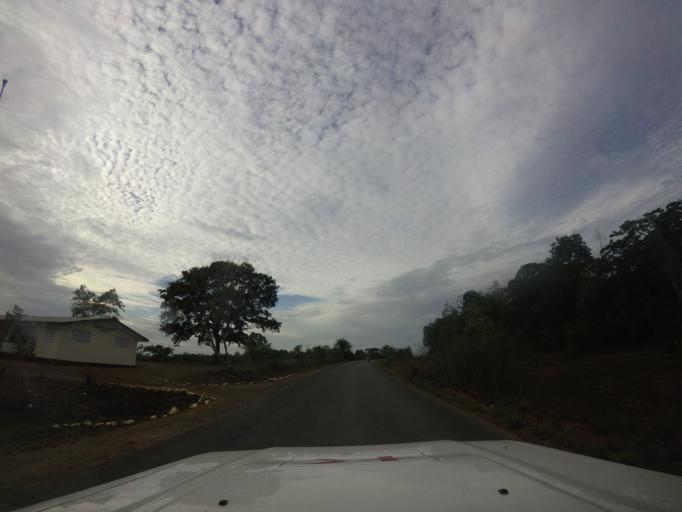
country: LR
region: Bomi
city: Tubmanburg
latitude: 6.7008
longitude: -10.8734
